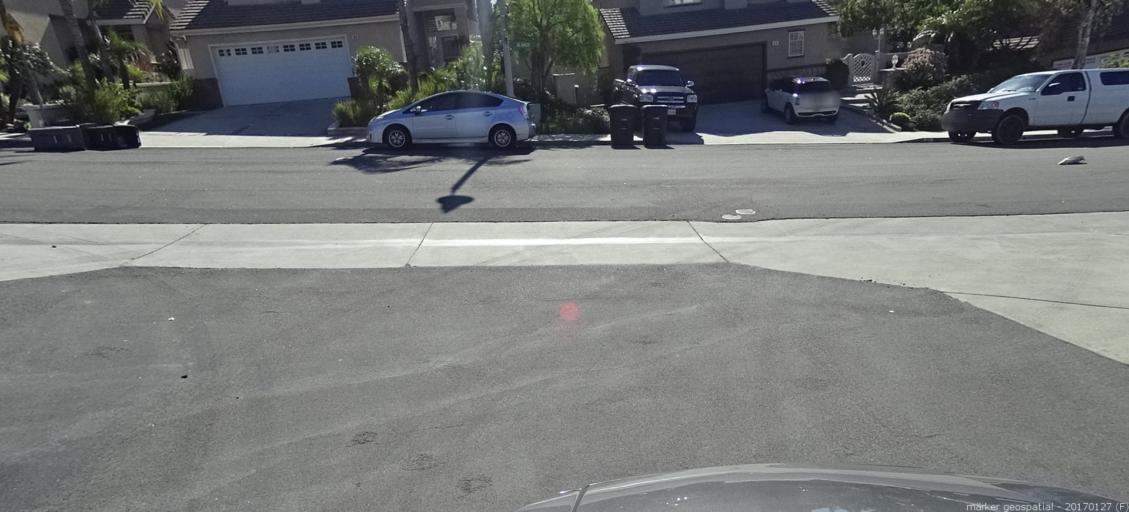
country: US
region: California
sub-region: Orange County
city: Foothill Ranch
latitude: 33.6845
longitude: -117.6637
